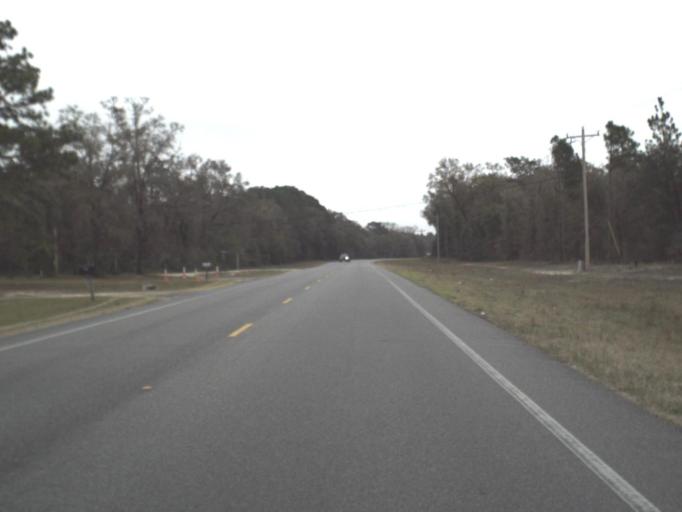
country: US
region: Florida
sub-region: Wakulla County
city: Crawfordville
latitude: 30.1293
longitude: -84.3572
